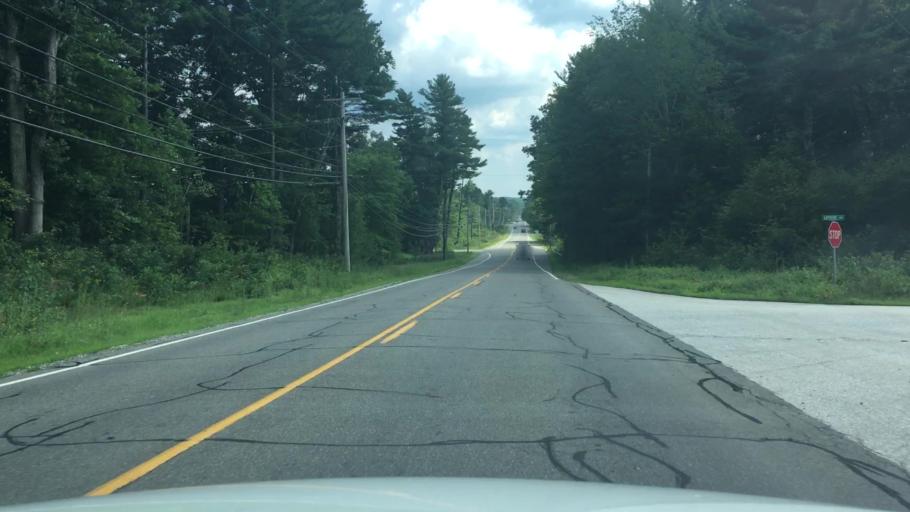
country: US
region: New Hampshire
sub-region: Rockingham County
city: Auburn
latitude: 42.9580
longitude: -71.3571
